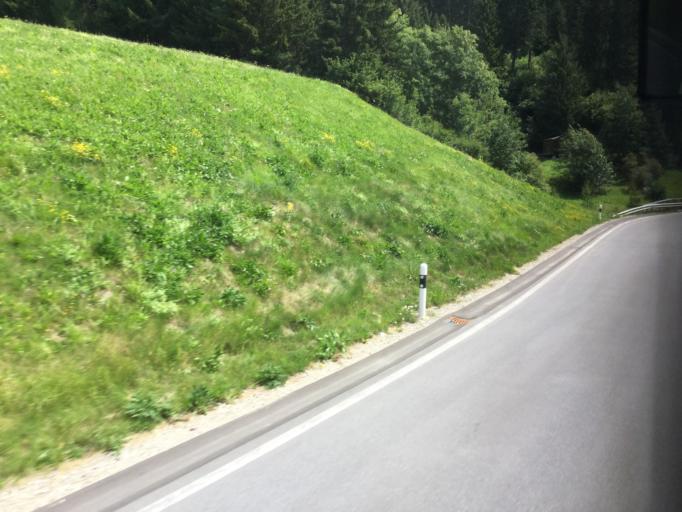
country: CH
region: Grisons
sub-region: Albula District
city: Tiefencastel
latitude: 46.6254
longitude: 9.5865
